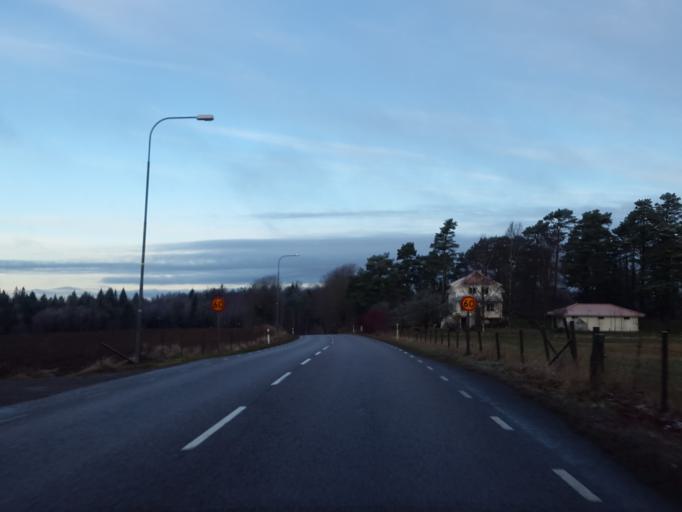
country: SE
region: Vaestra Goetaland
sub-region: Boras Kommun
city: Sjomarken
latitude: 57.7712
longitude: 12.8169
